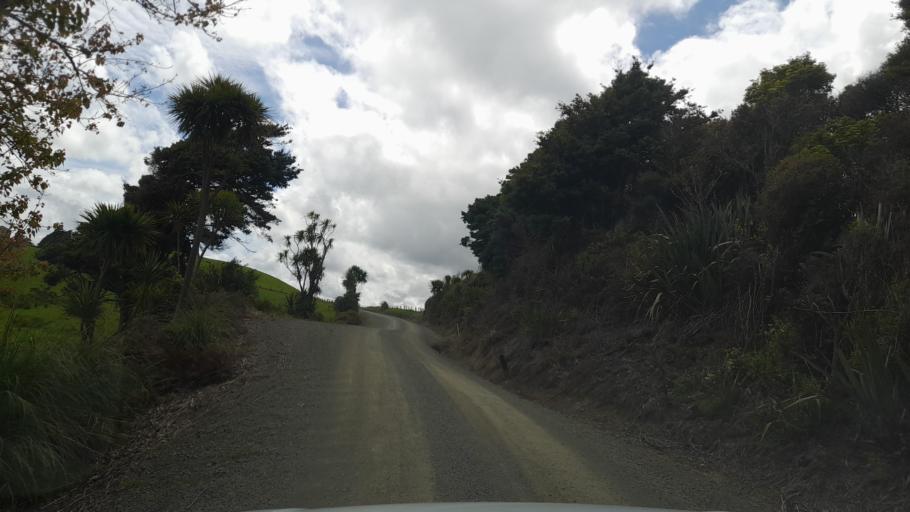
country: NZ
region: Auckland
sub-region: Auckland
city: Wellsford
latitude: -36.1915
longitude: 174.3394
